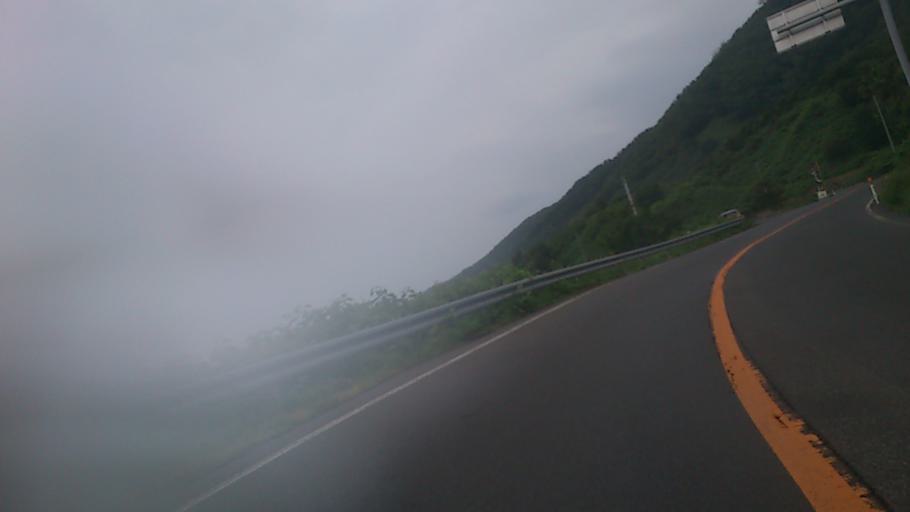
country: JP
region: Akita
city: Noshiromachi
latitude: 40.4290
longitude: 139.9400
